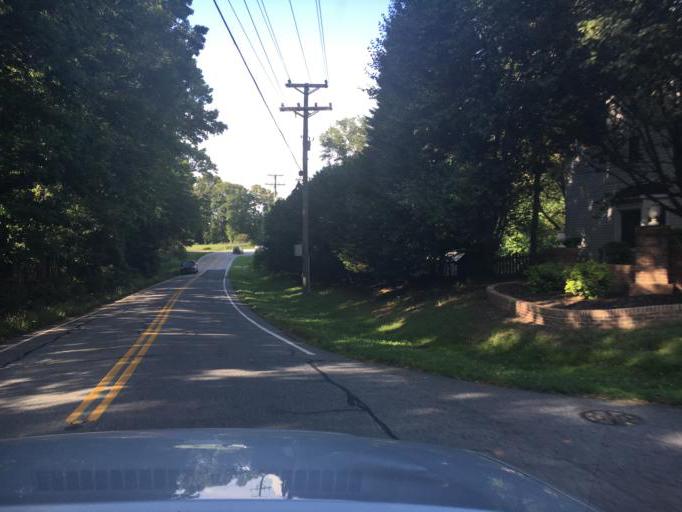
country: US
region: South Carolina
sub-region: Greenville County
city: Five Forks
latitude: 34.7915
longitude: -82.2320
